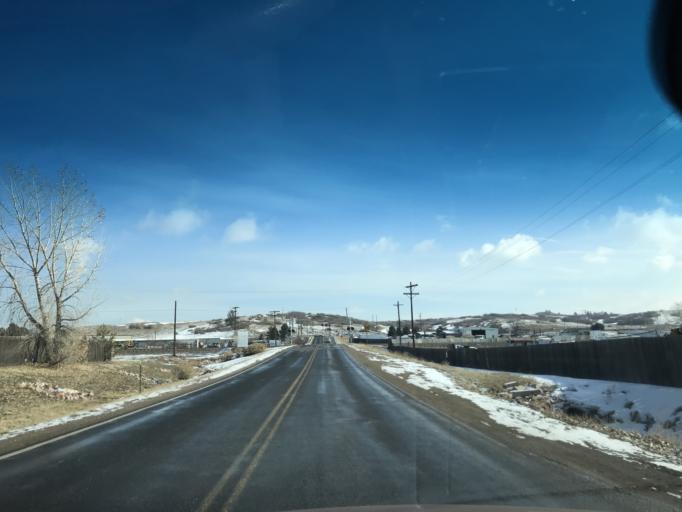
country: US
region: Colorado
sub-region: Douglas County
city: Highlands Ranch
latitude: 39.4710
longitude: -104.9928
